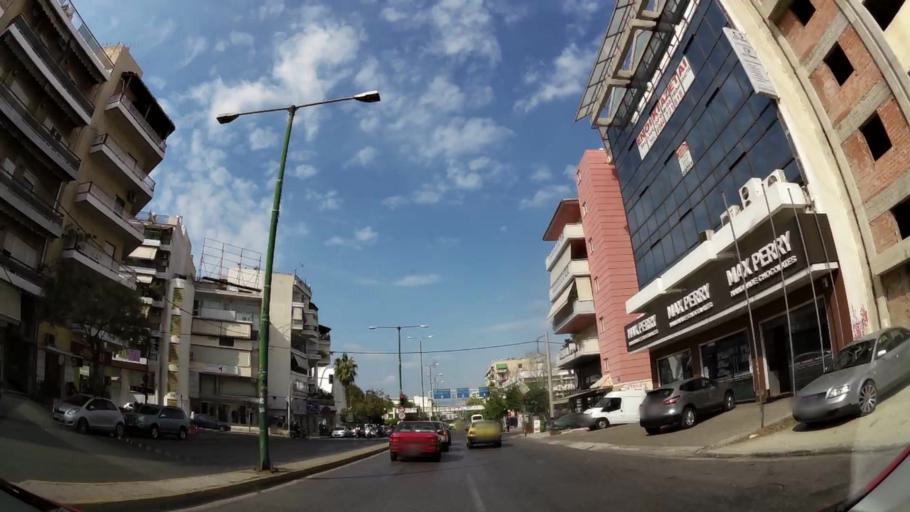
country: GR
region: Attica
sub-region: Nomarchia Athinas
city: Dhafni
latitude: 37.9562
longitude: 23.7245
